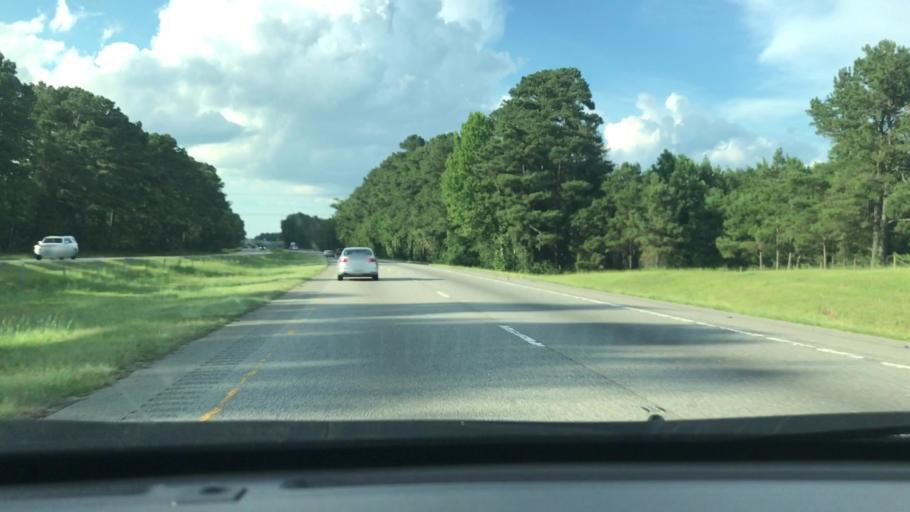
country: US
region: North Carolina
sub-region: Robeson County
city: Saint Pauls
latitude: 34.8542
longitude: -78.9666
